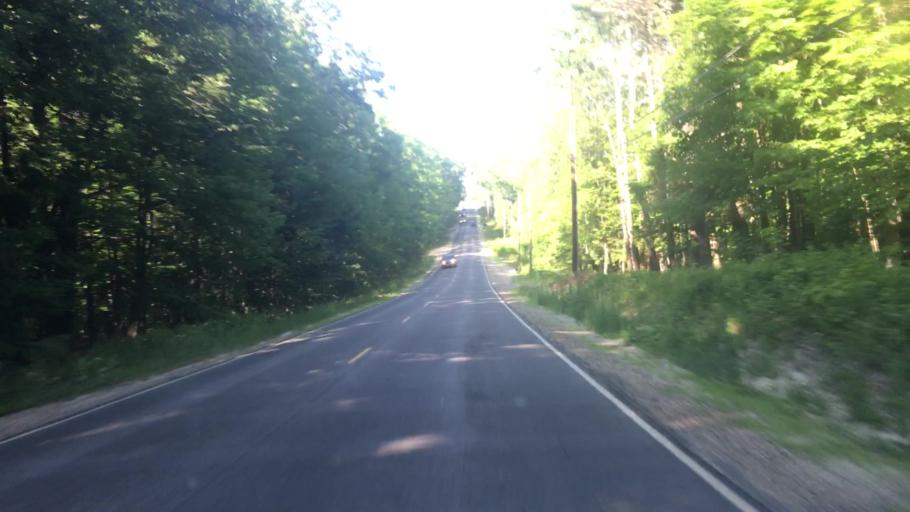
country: US
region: Maine
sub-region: York County
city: Buxton
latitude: 43.7275
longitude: -70.5592
